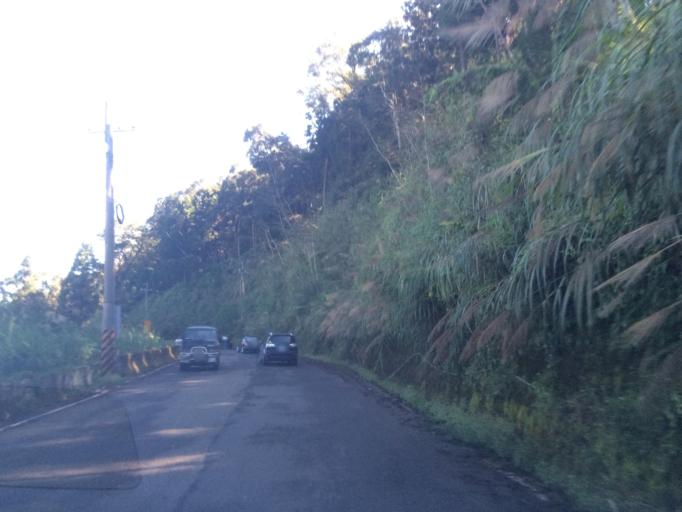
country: TW
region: Taiwan
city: Lugu
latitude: 23.6553
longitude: 120.7811
